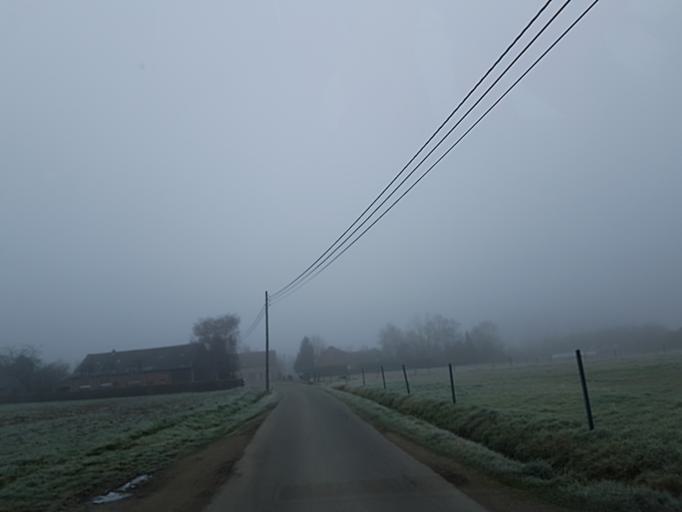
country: BE
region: Flanders
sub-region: Provincie Vlaams-Brabant
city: Zemst
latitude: 50.9919
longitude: 4.4315
